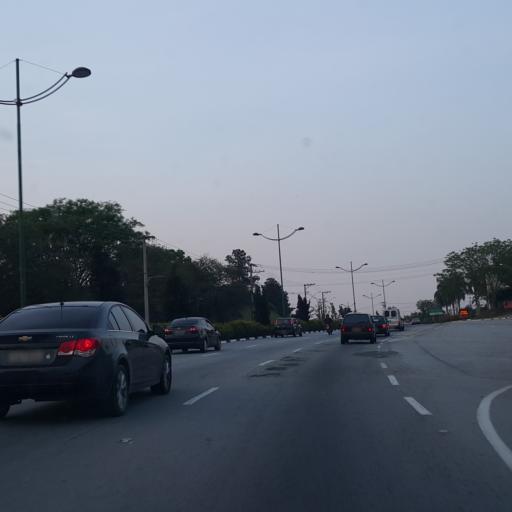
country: BR
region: Sao Paulo
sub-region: Vinhedo
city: Vinhedo
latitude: -23.0446
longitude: -46.9849
